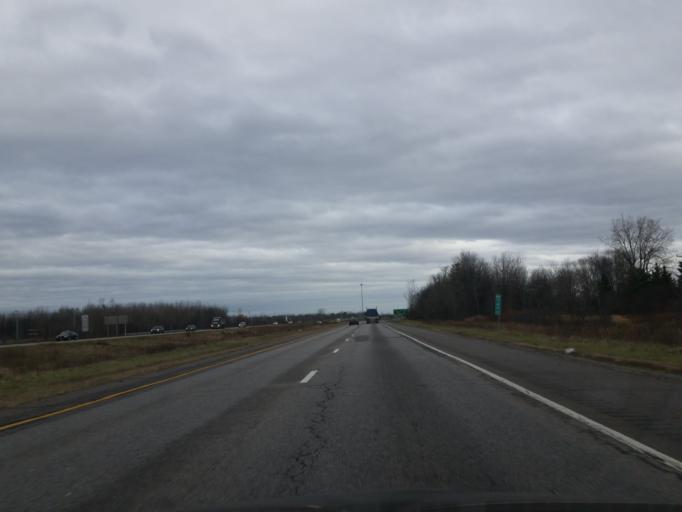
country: CA
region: Quebec
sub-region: Outaouais
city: Gatineau
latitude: 45.5102
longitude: -75.6548
